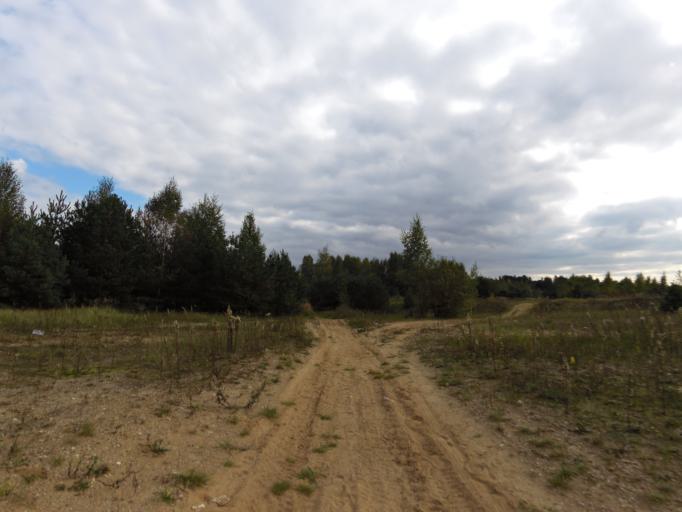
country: LT
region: Vilnius County
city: Pilaite
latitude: 54.7063
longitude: 25.1634
